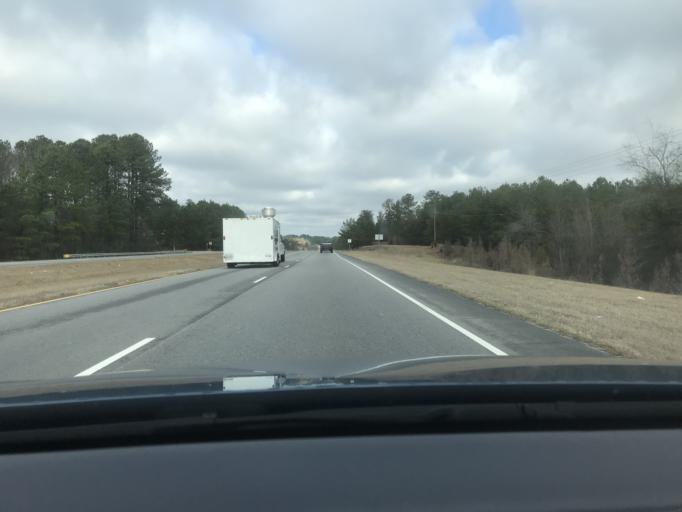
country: US
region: North Carolina
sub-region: Cumberland County
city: Spring Lake
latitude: 35.2916
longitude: -79.0782
